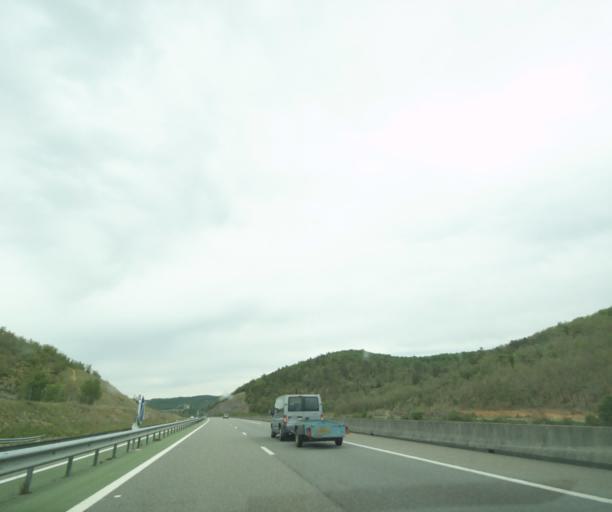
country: FR
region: Midi-Pyrenees
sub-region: Departement du Lot
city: Cahors
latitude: 44.4413
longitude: 1.5049
